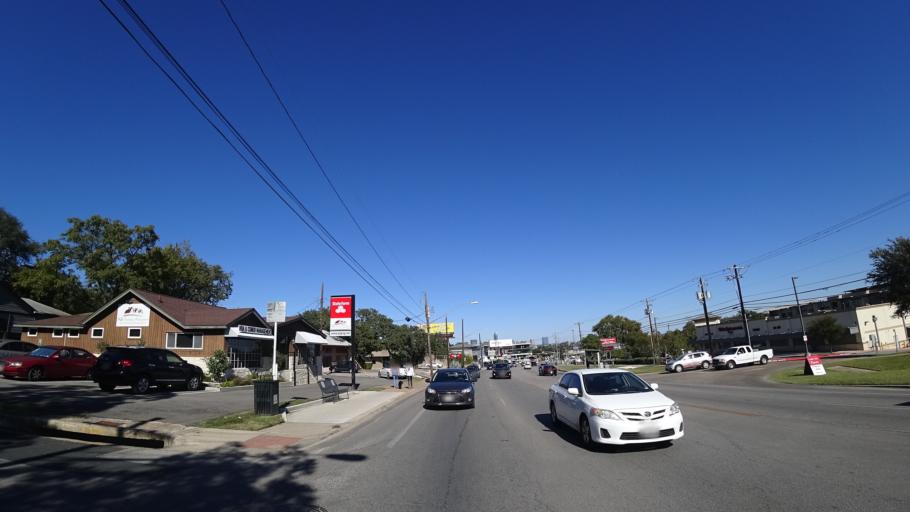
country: US
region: Texas
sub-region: Travis County
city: Rollingwood
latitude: 30.2462
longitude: -97.7788
